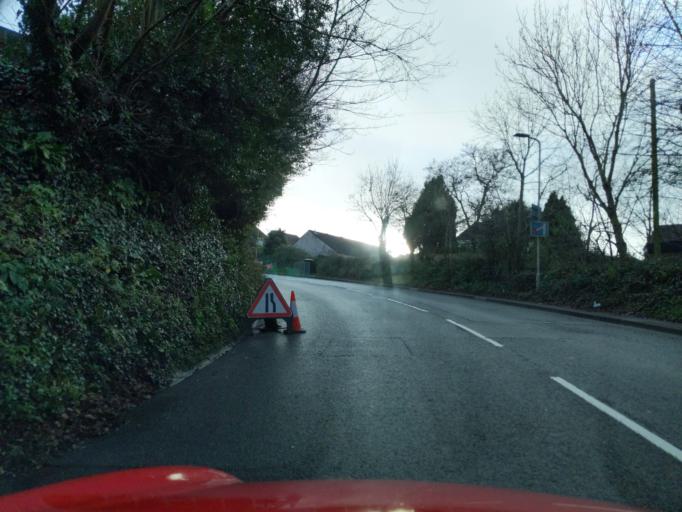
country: GB
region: England
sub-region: Plymouth
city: Plymstock
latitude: 50.3532
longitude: -4.0749
